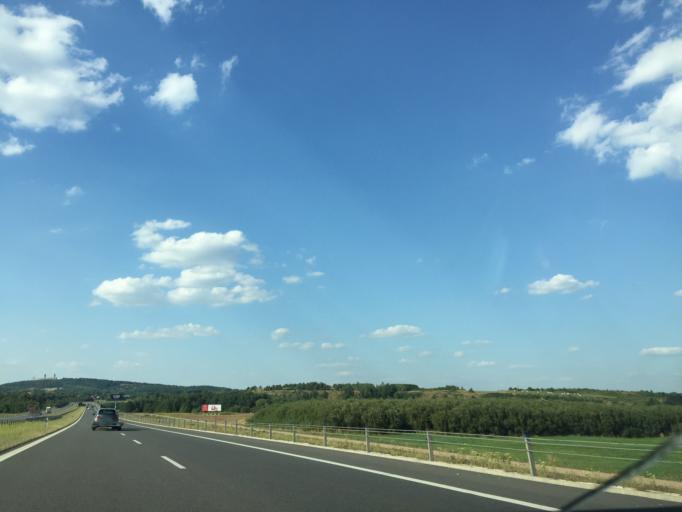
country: PL
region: Swietokrzyskie
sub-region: Powiat kielecki
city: Checiny
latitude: 50.7662
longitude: 20.4644
